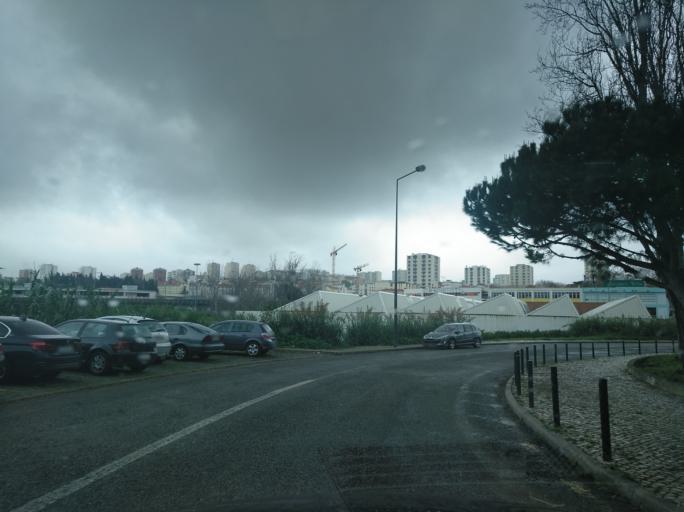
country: PT
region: Lisbon
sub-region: Loures
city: Moscavide
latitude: 38.7694
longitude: -9.1029
